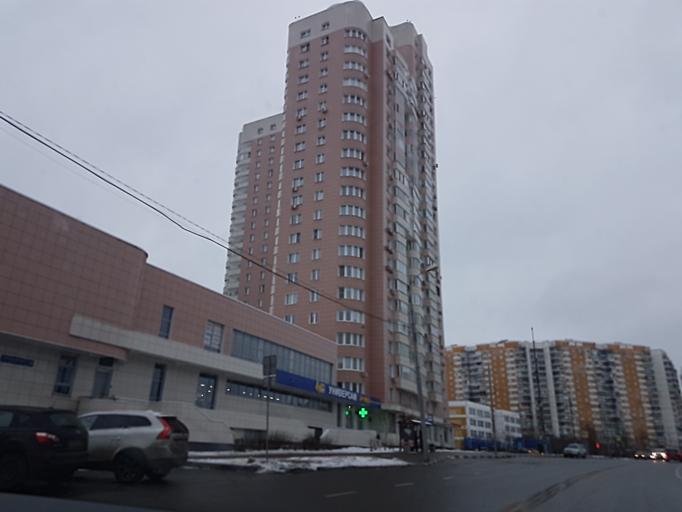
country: RU
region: Moskovskaya
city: Pavshino
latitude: 55.8304
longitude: 37.3544
